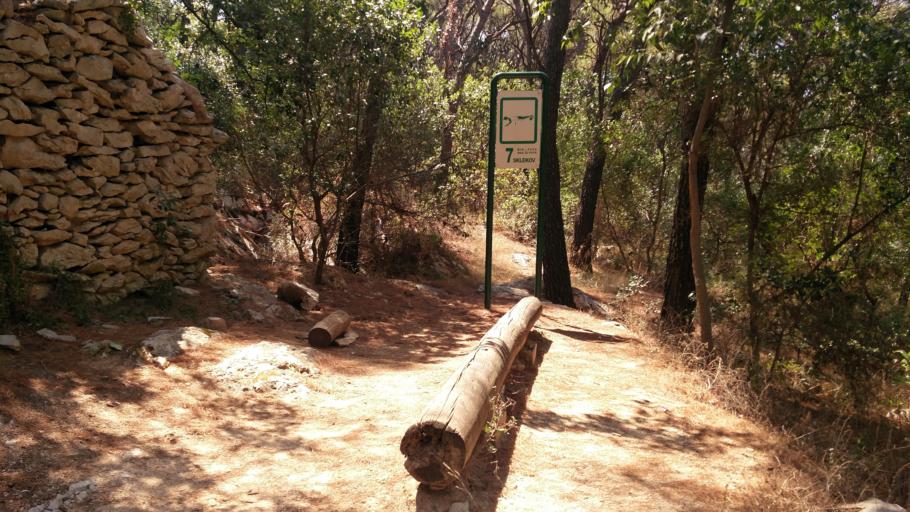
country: HR
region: Splitsko-Dalmatinska
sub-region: Grad Split
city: Split
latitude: 43.5118
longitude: 16.4011
